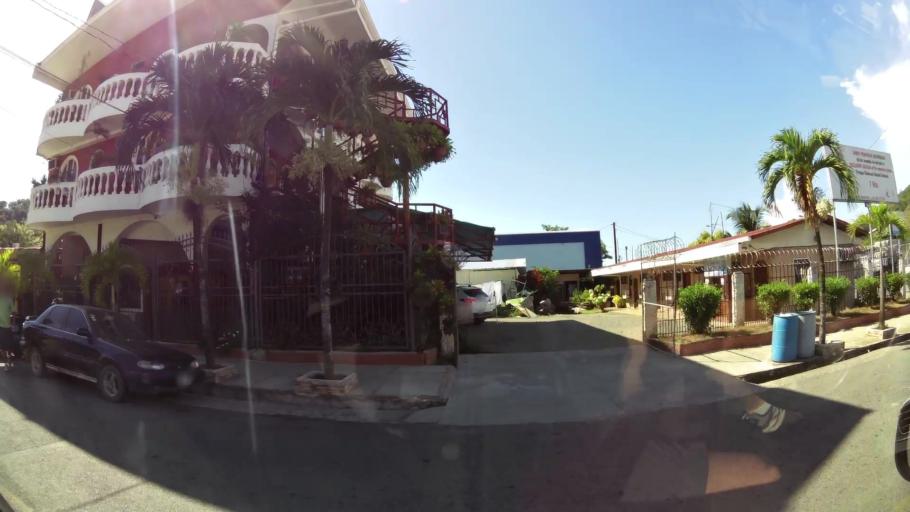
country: CR
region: Puntarenas
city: Quepos
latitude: 9.4313
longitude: -84.1601
